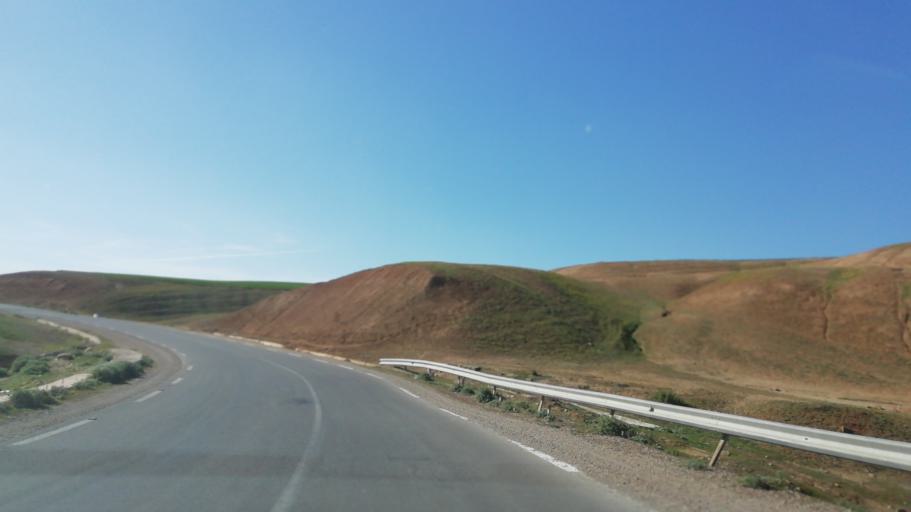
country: DZ
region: Mascara
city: Oued el Abtal
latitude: 35.4494
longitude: 0.8116
